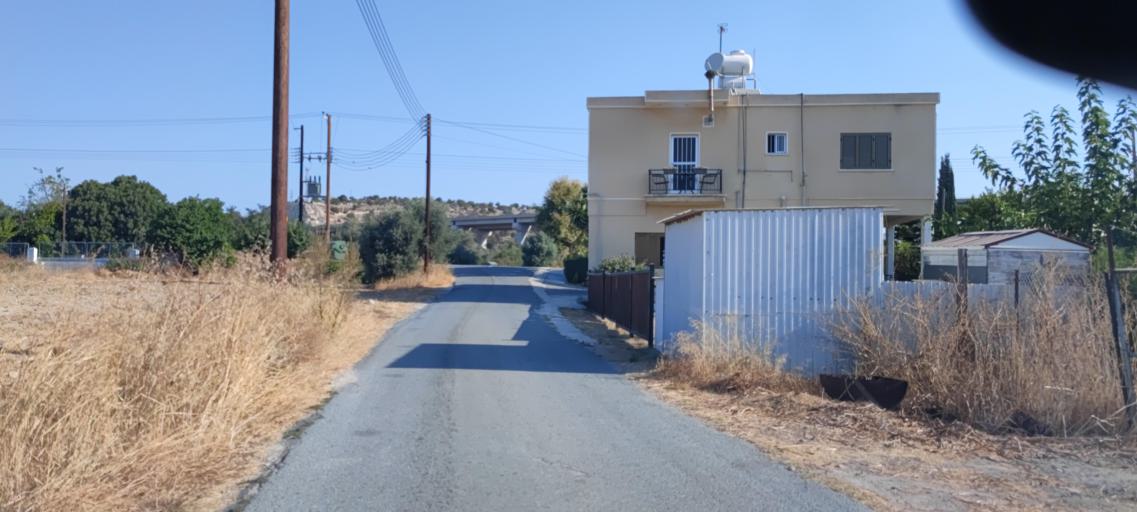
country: CY
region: Limassol
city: Sotira
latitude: 34.6757
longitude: 32.7953
